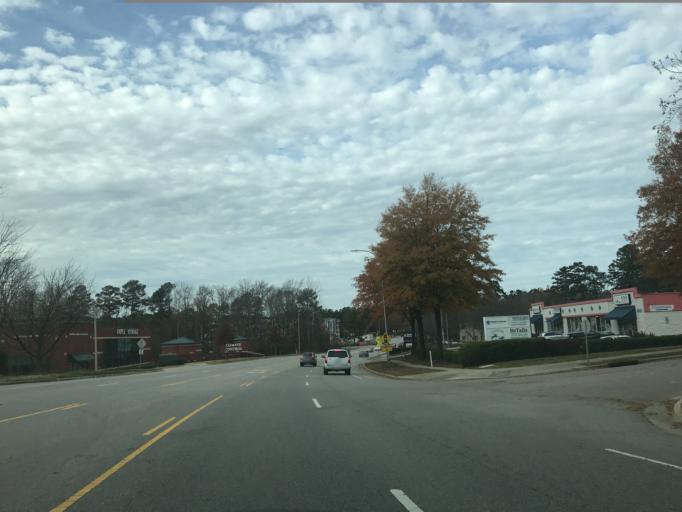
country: US
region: North Carolina
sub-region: Wake County
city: Raleigh
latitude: 35.8558
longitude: -78.5923
